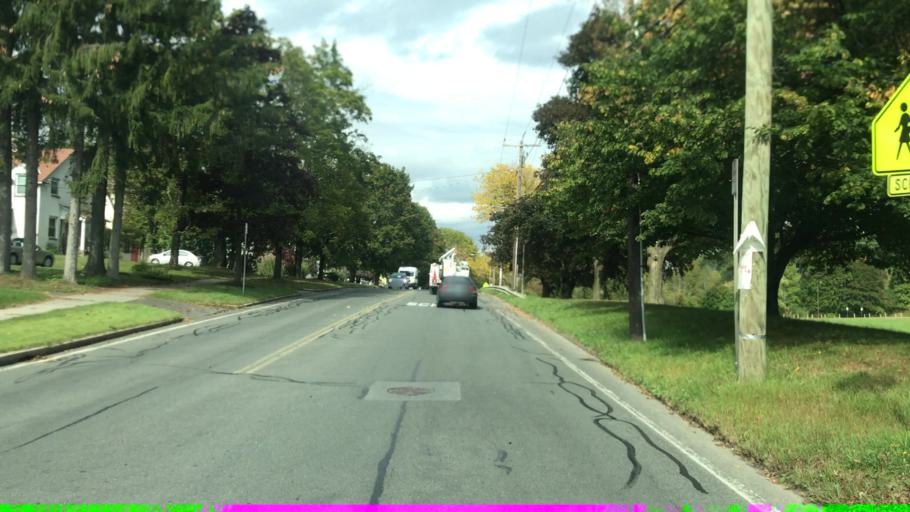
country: US
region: Massachusetts
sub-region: Berkshire County
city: Pittsfield
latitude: 42.4656
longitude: -73.2459
